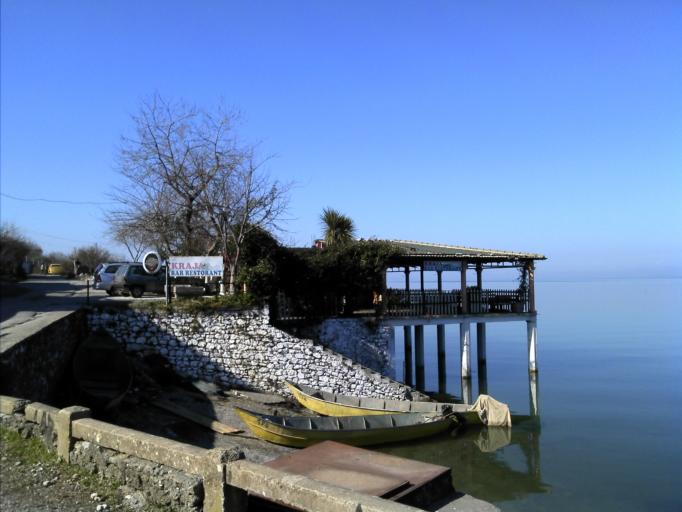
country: AL
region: Shkoder
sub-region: Rrethi i Shkodres
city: Berdica e Madhe
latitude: 42.0595
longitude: 19.4534
